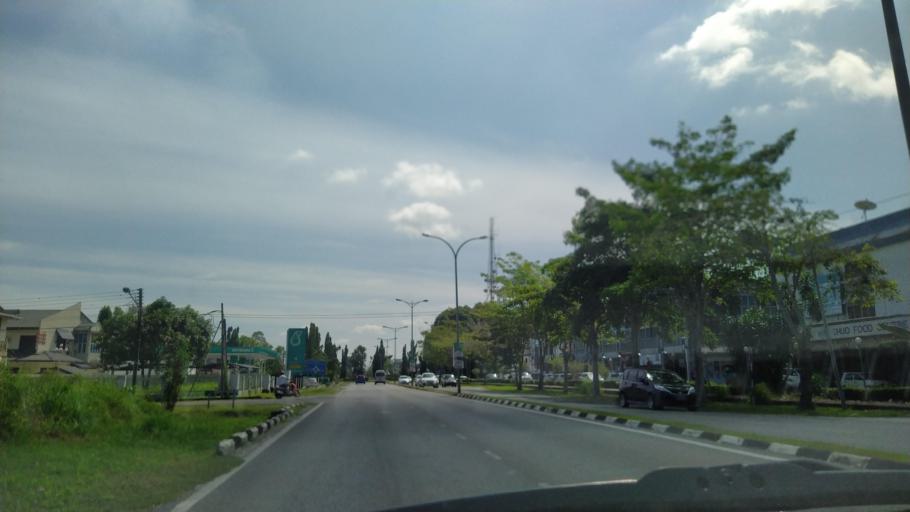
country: MY
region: Sarawak
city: Sibu
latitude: 2.3106
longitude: 111.8301
